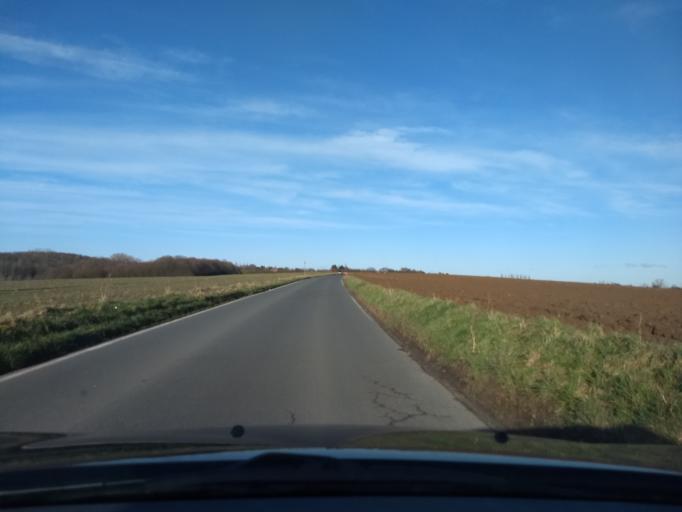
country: BE
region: Wallonia
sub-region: Province du Brabant Wallon
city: Ittre
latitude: 50.6532
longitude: 4.2692
